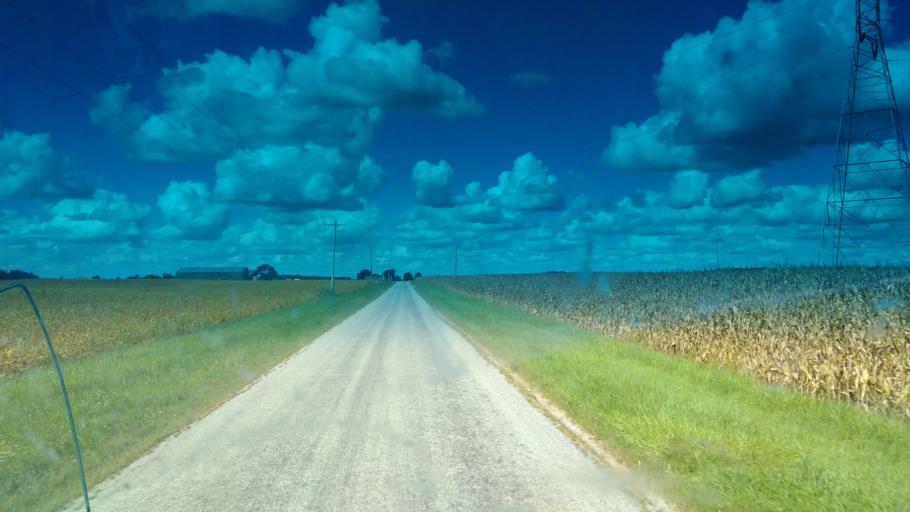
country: US
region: Ohio
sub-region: Union County
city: Richwood
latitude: 40.4417
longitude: -83.4924
